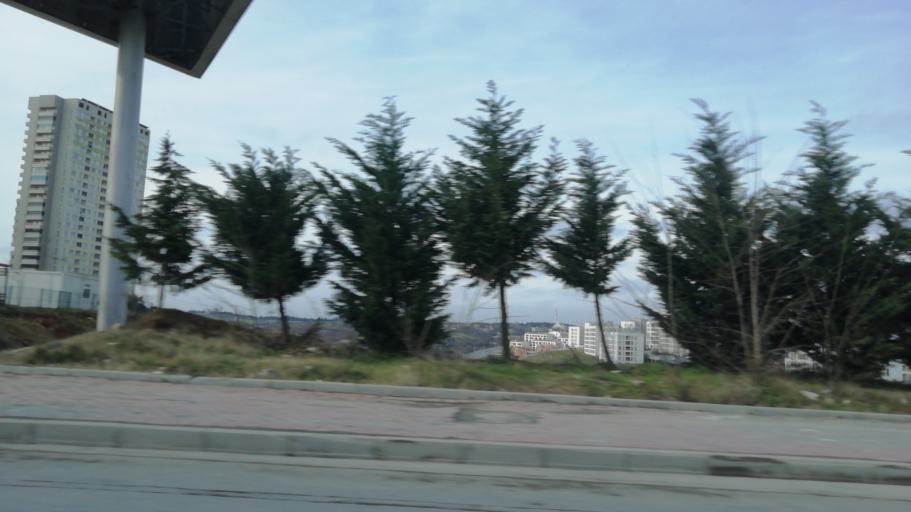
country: TR
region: Istanbul
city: Basaksehir
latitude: 41.1296
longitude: 28.7796
